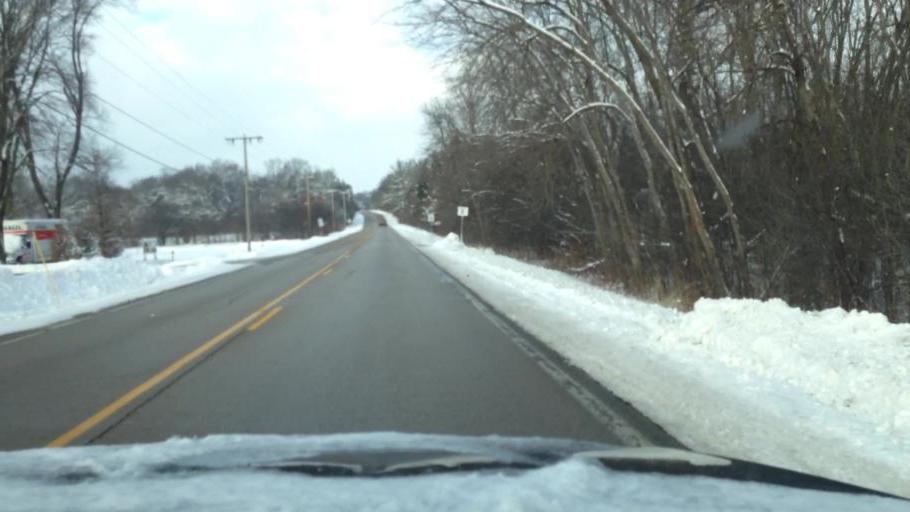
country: US
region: Wisconsin
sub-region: Waukesha County
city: Eagle
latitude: 42.8587
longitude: -88.4313
